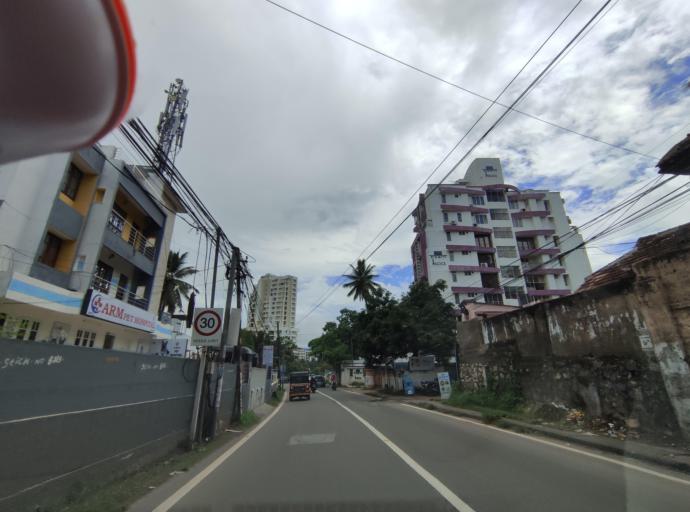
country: IN
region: Kerala
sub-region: Thiruvananthapuram
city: Thiruvananthapuram
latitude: 8.4933
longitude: 76.9682
